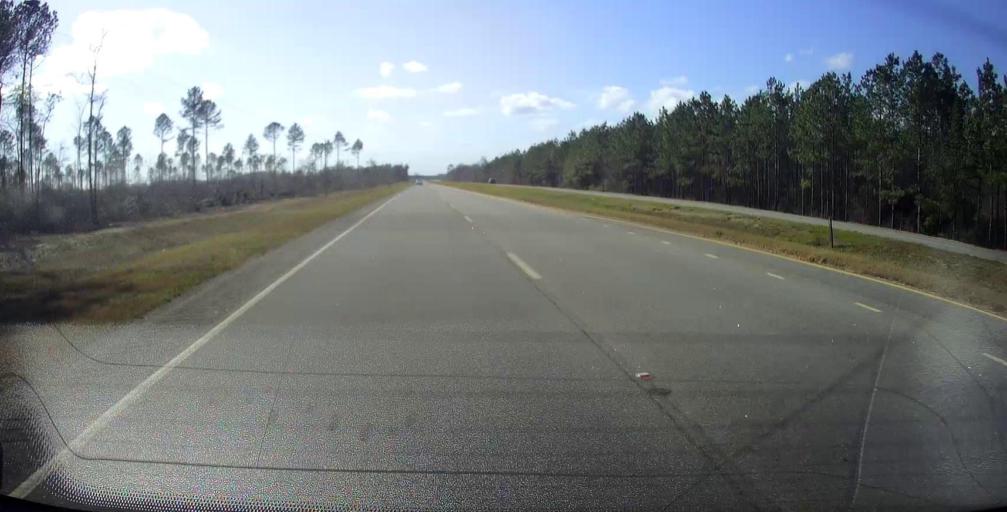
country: US
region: Georgia
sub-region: Dodge County
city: Eastman
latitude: 32.2038
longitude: -83.3106
